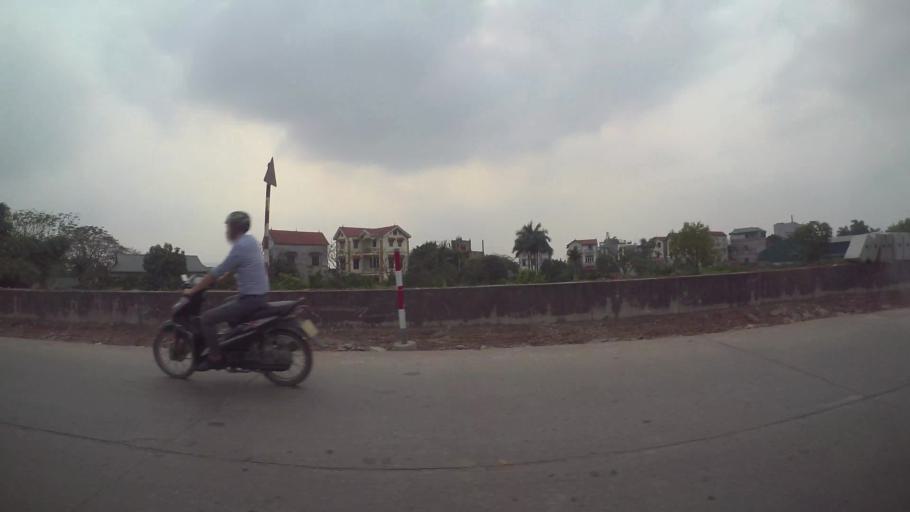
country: VN
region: Ha Noi
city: Trau Quy
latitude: 21.0087
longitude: 105.9053
